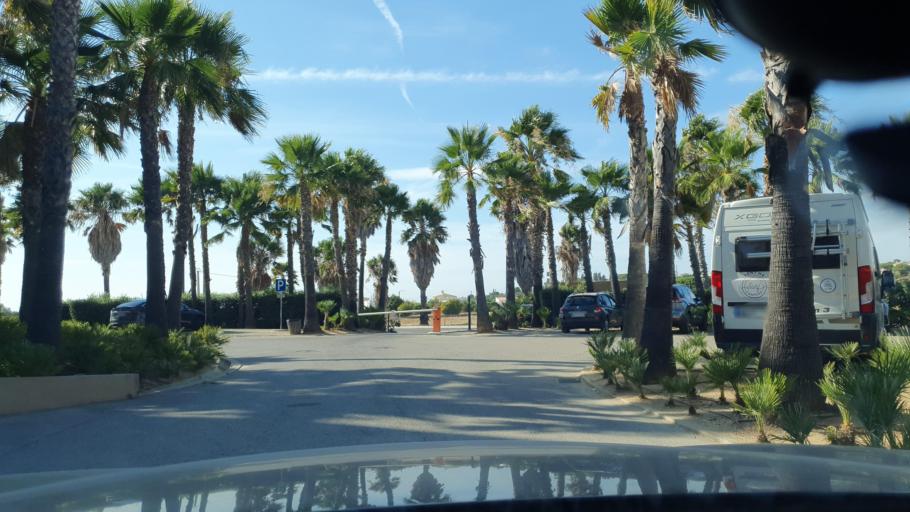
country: PT
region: Faro
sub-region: Silves
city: Armacao de Pera
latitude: 37.0948
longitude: -8.3199
